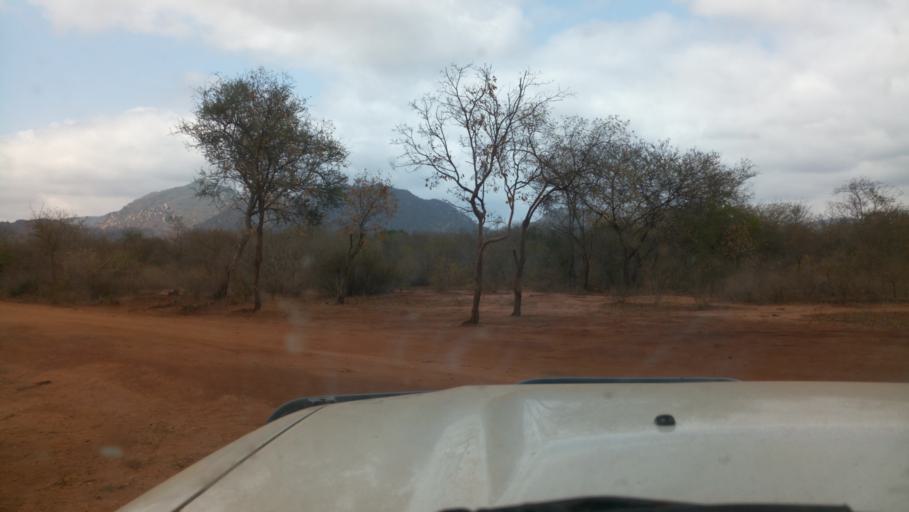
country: KE
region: Kitui
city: Kitui
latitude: -1.8391
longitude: 38.3370
